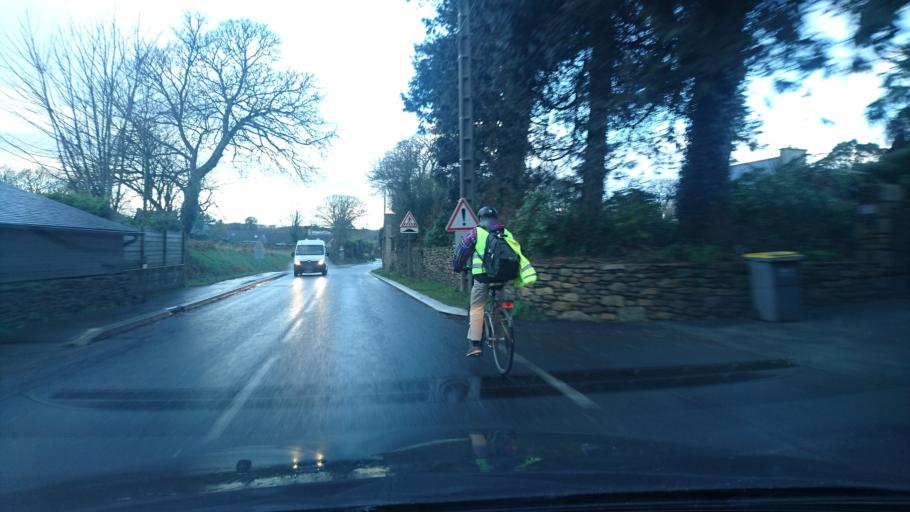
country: FR
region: Brittany
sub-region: Departement du Finistere
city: Guilers
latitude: 48.3984
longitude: -4.5395
